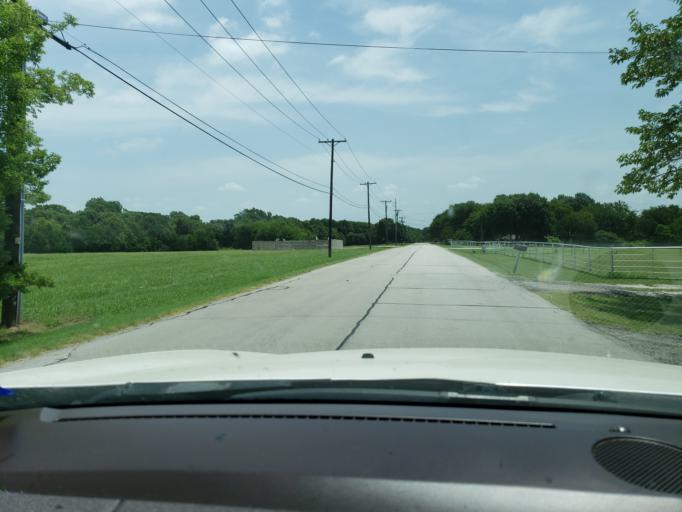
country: US
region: Texas
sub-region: Dallas County
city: Rowlett
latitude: 32.8965
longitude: -96.5546
